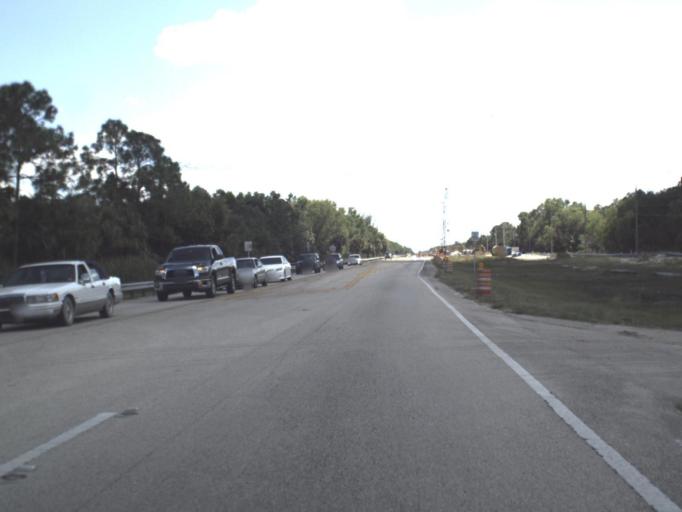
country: US
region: Florida
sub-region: Collier County
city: Lely Resort
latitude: 26.0604
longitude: -81.6946
